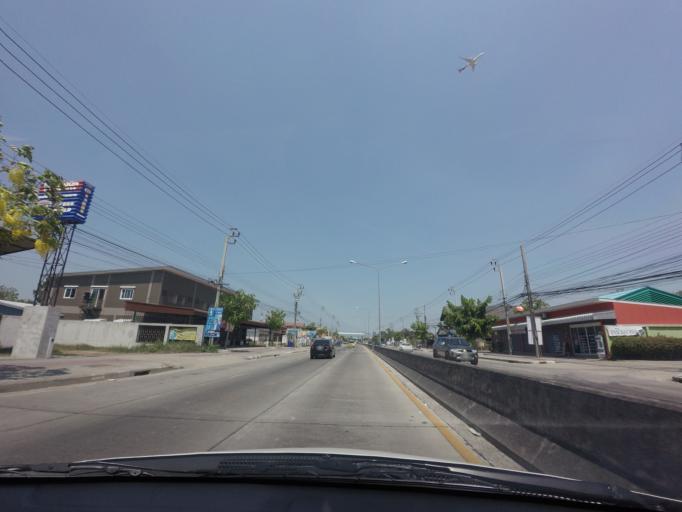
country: TH
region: Bangkok
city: Khlong Sam Wa
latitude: 13.8314
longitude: 100.7716
